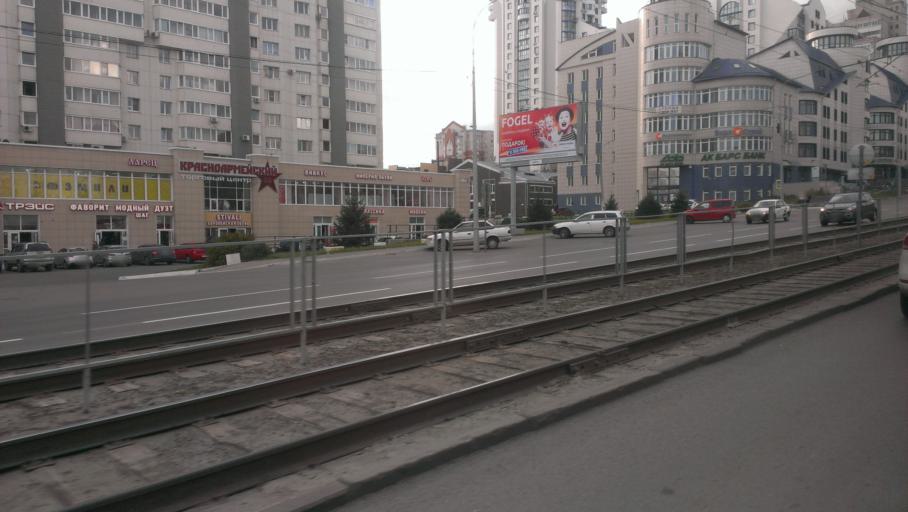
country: RU
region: Altai Krai
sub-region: Gorod Barnaulskiy
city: Barnaul
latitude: 53.3395
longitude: 83.7725
